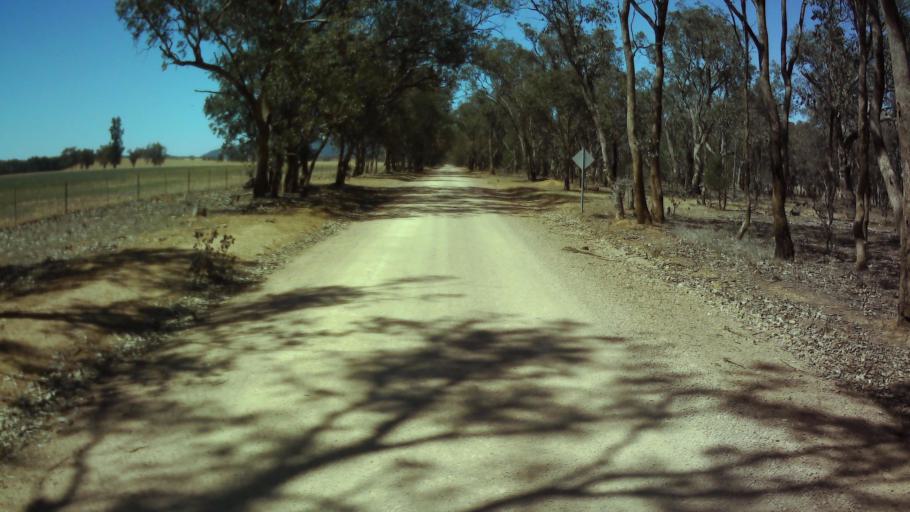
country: AU
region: New South Wales
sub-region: Weddin
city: Grenfell
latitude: -33.9087
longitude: 148.0802
